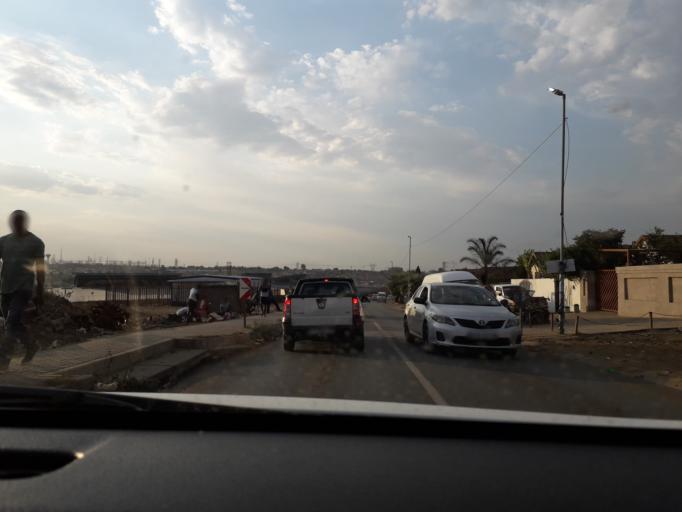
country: ZA
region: Gauteng
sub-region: Ekurhuleni Metropolitan Municipality
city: Tembisa
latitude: -26.0382
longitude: 28.1946
